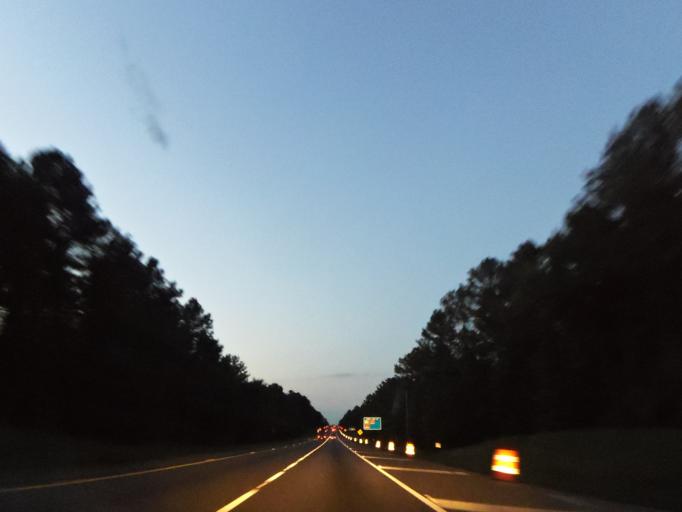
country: US
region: Tennessee
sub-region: Bradley County
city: Hopewell
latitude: 35.2583
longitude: -84.8337
